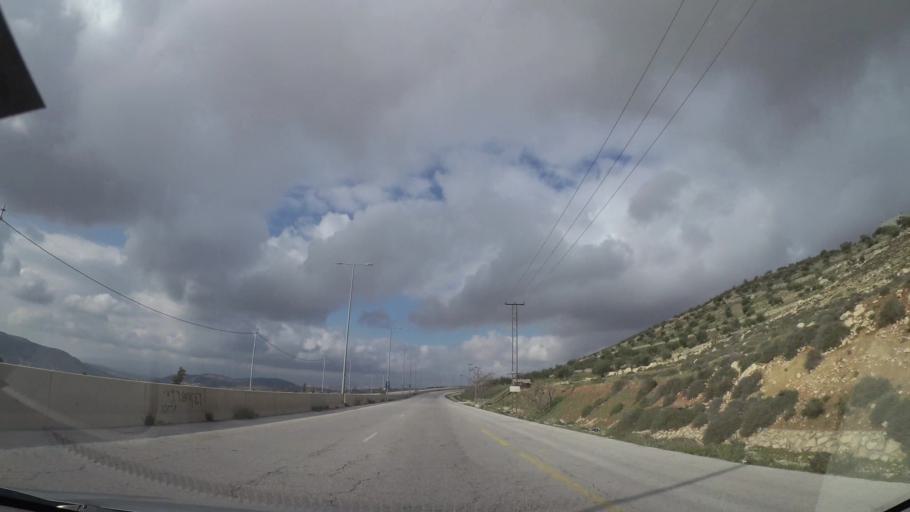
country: JO
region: Amman
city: Al Jubayhah
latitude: 32.0763
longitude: 35.8788
